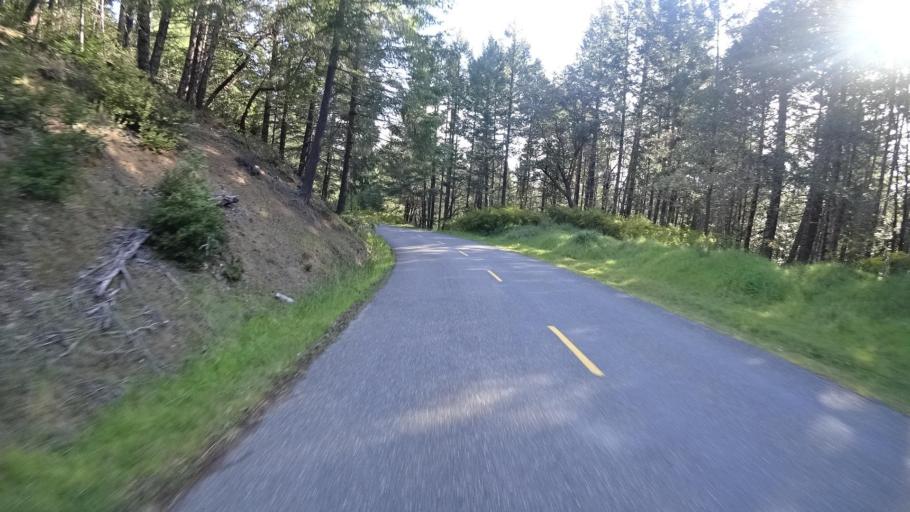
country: US
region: California
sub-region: Humboldt County
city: Rio Dell
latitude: 40.3265
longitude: -124.0416
